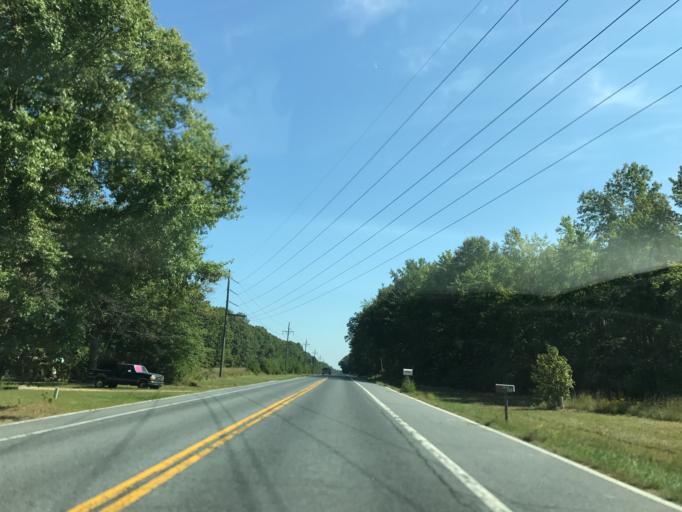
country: US
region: Maryland
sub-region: Queen Anne's County
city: Kingstown
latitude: 39.2638
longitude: -75.8917
